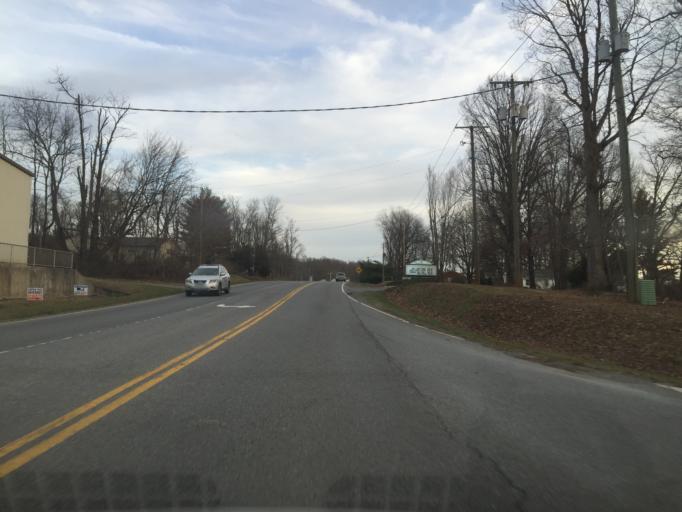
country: US
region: Virginia
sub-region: Bedford County
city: Forest
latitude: 37.3591
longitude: -79.2845
